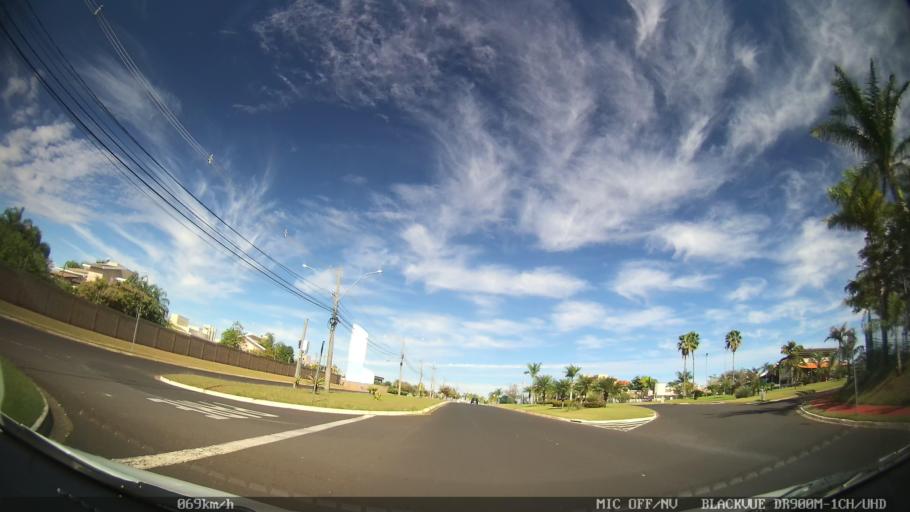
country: BR
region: Sao Paulo
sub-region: Bady Bassitt
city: Bady Bassitt
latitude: -20.8227
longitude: -49.4818
